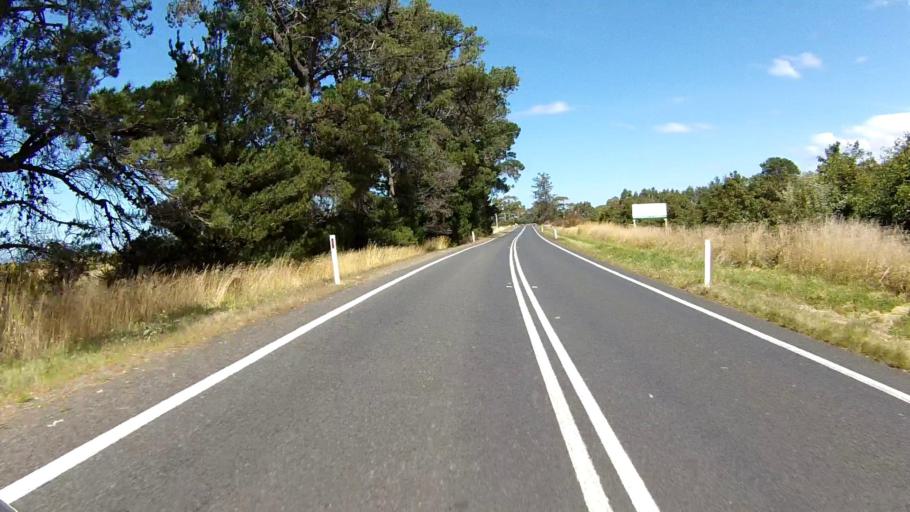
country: AU
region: Tasmania
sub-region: Break O'Day
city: St Helens
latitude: -42.0651
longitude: 148.0637
